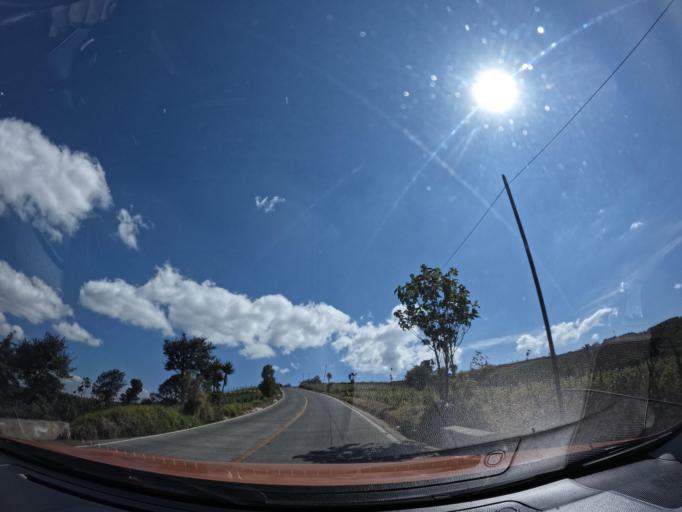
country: GT
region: Chimaltenango
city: Patzun
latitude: 14.6650
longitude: -91.0557
